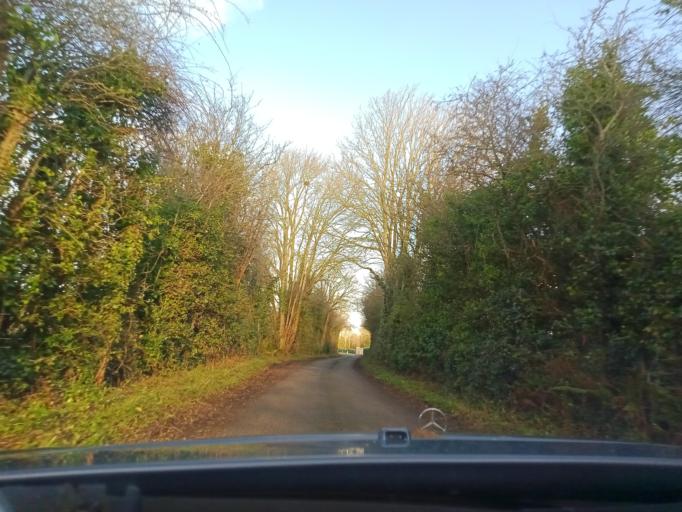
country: IE
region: Leinster
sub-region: Kilkenny
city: Callan
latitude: 52.5013
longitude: -7.3541
